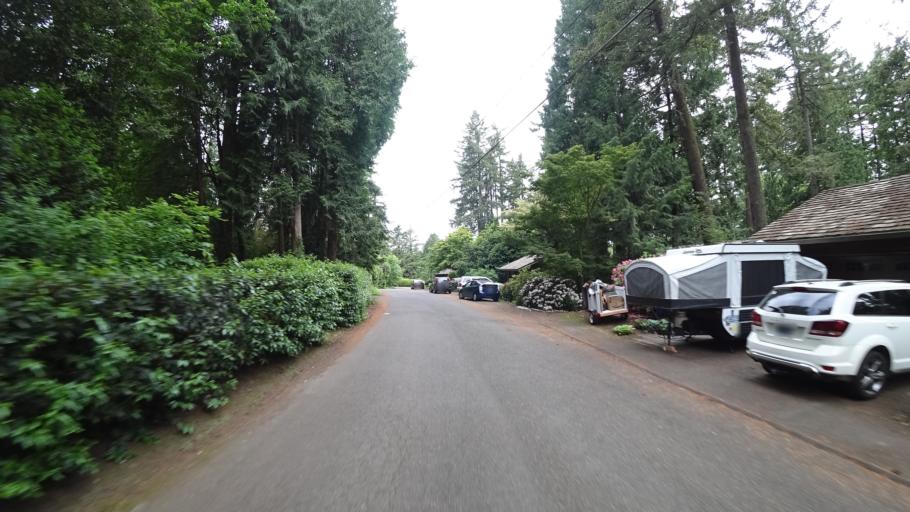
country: US
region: Oregon
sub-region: Washington County
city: Garden Home-Whitford
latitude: 45.4701
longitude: -122.7503
